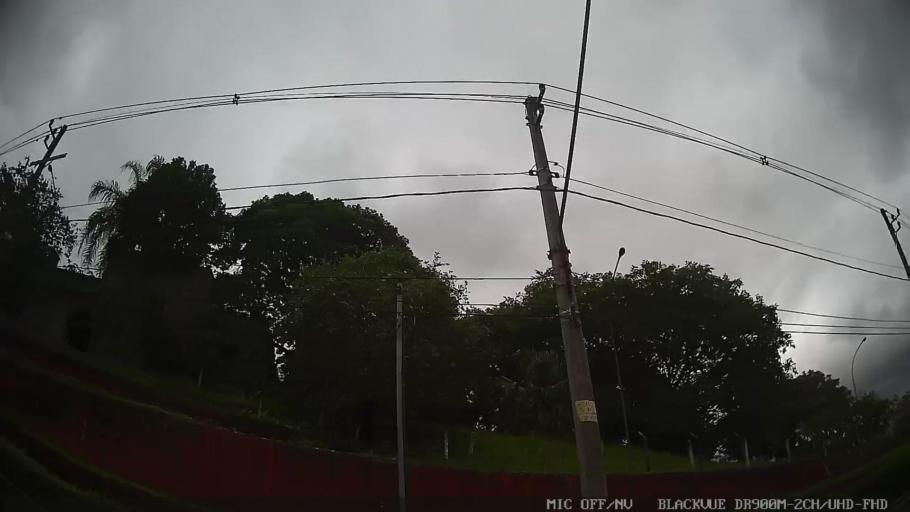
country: BR
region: Sao Paulo
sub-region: Osasco
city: Osasco
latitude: -23.5125
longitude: -46.7248
